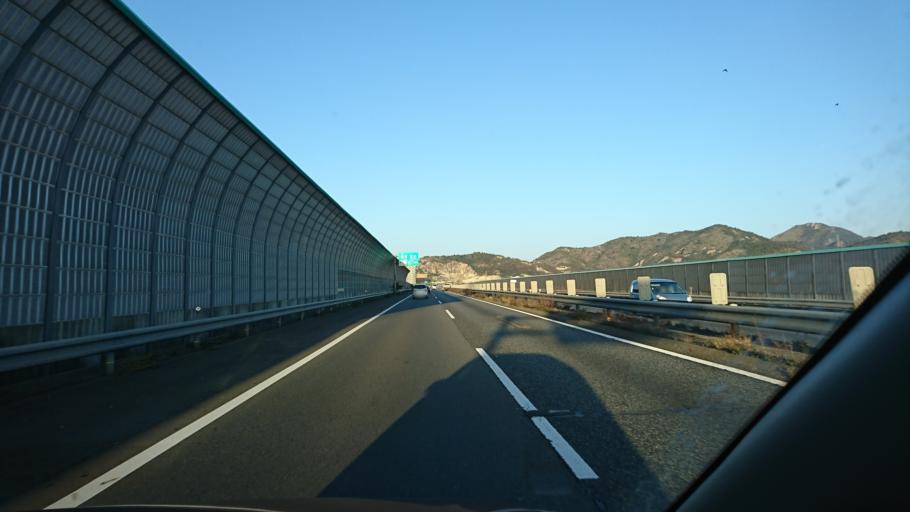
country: JP
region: Hyogo
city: Kakogawacho-honmachi
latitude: 34.7890
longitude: 134.8141
